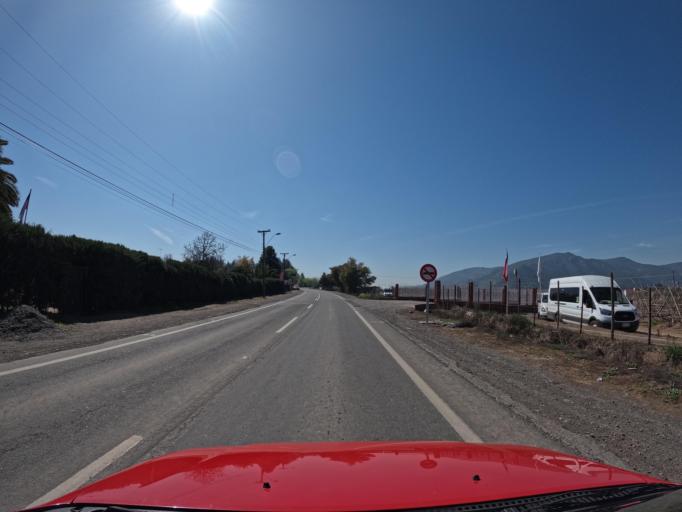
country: CL
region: Maule
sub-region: Provincia de Curico
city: Rauco
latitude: -35.0349
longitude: -71.4464
